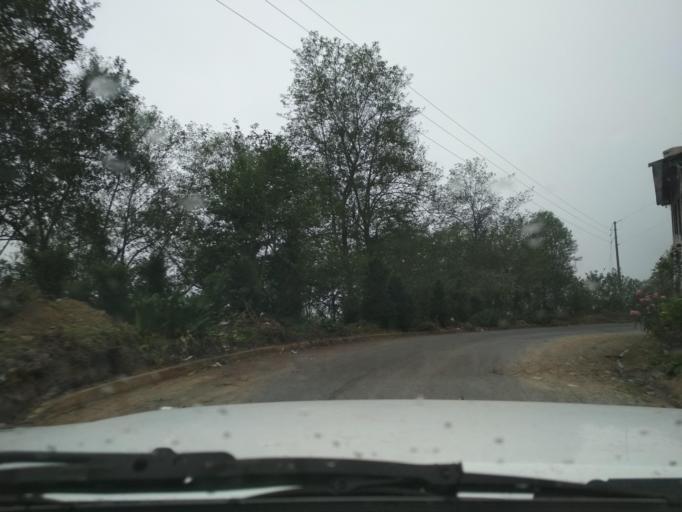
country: MX
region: Veracruz
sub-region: La Perla
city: Metlac Hernandez (Metlac Primero)
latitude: 18.9497
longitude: -97.1638
